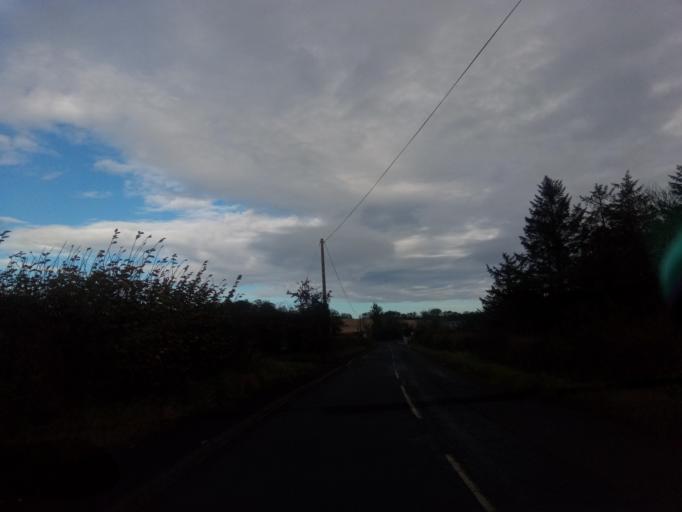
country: GB
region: Scotland
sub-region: The Scottish Borders
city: Eyemouth
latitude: 55.8648
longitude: -2.0968
